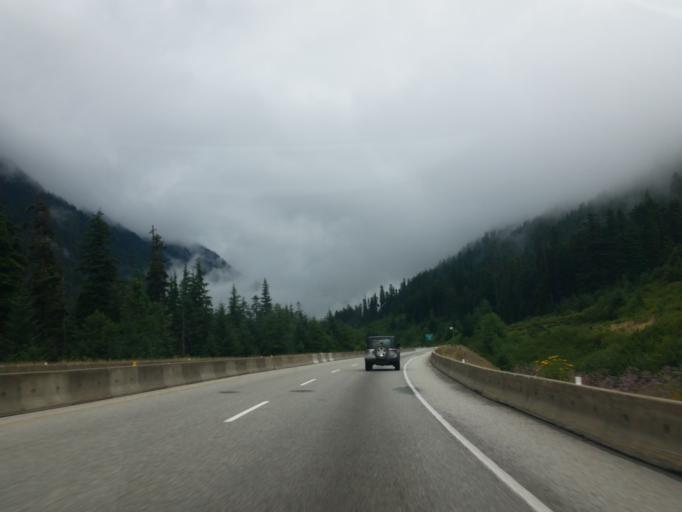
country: CA
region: British Columbia
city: Hope
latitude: 49.5629
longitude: -121.1864
